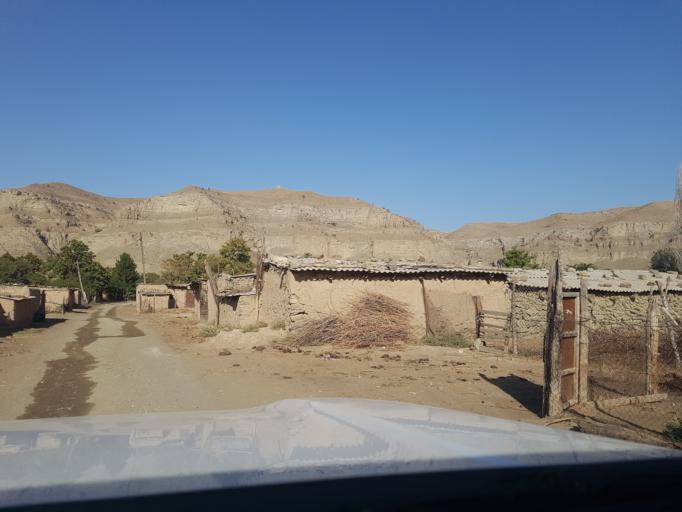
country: TM
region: Balkan
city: Magtymguly
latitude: 38.3012
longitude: 56.7464
